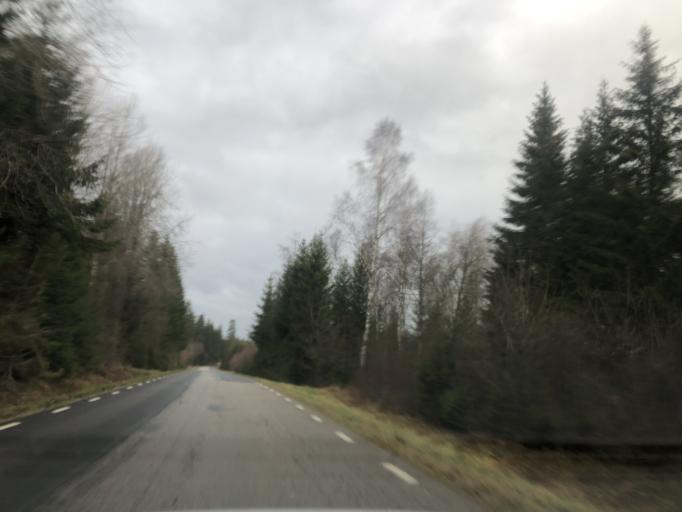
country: SE
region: Vaestra Goetaland
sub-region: Boras Kommun
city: Dalsjofors
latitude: 57.8139
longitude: 13.1988
